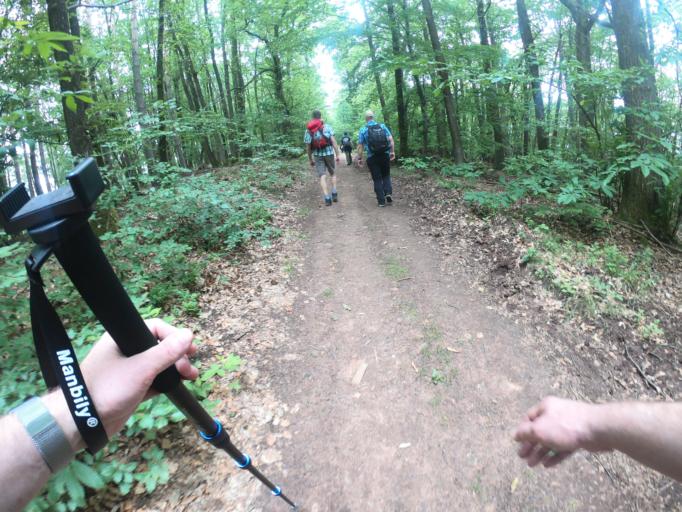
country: DE
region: Rheinland-Pfalz
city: Leinsweiler
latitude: 49.1905
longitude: 8.0106
